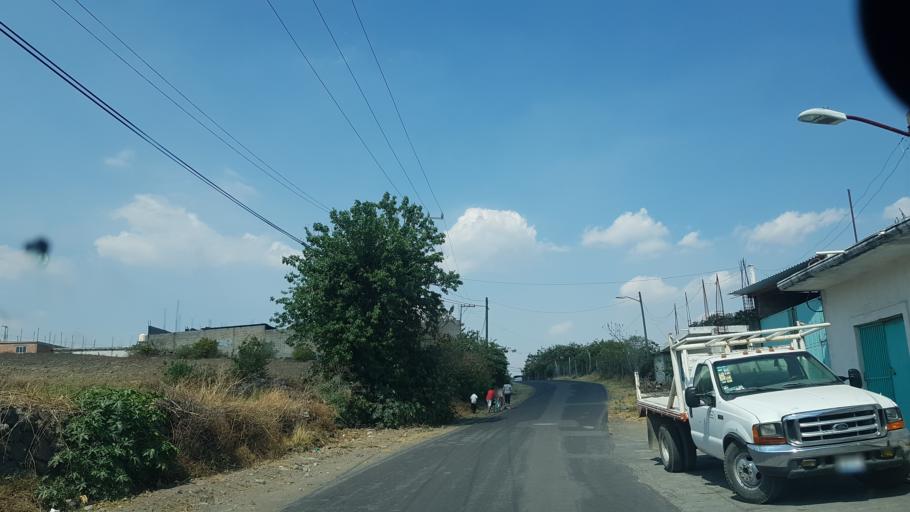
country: MX
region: Puebla
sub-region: Atlixco
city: San Pedro Benito Juarez
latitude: 18.9517
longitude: -98.5454
